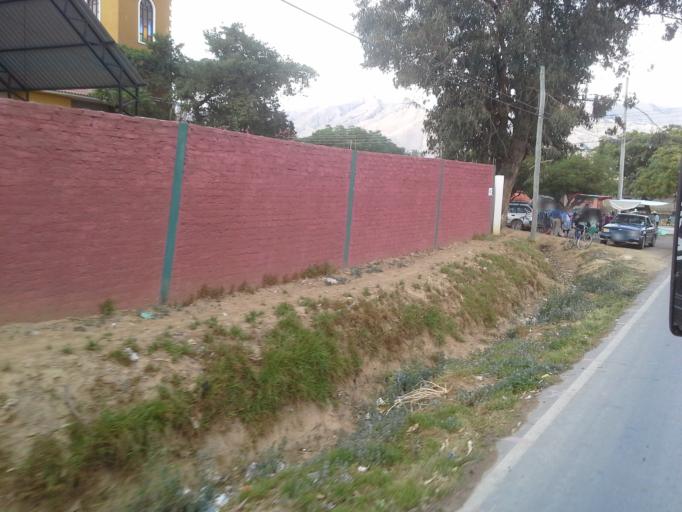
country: BO
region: Cochabamba
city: Tarata
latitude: -17.5636
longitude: -66.0097
